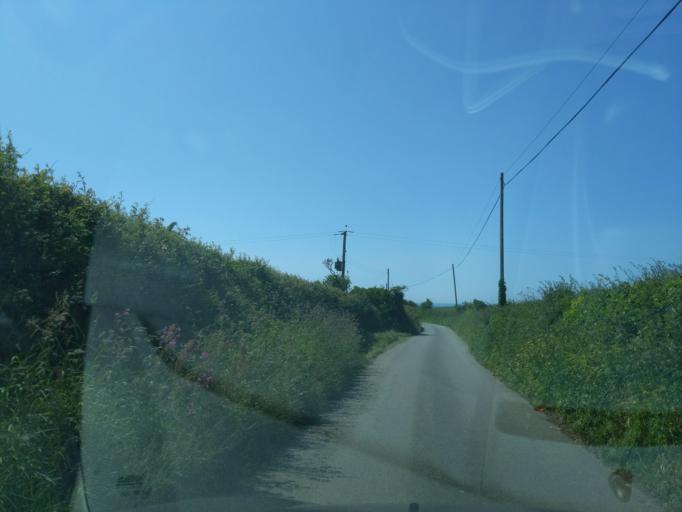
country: GB
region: England
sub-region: Cornwall
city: Wadebridge
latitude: 50.5837
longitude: -4.8445
